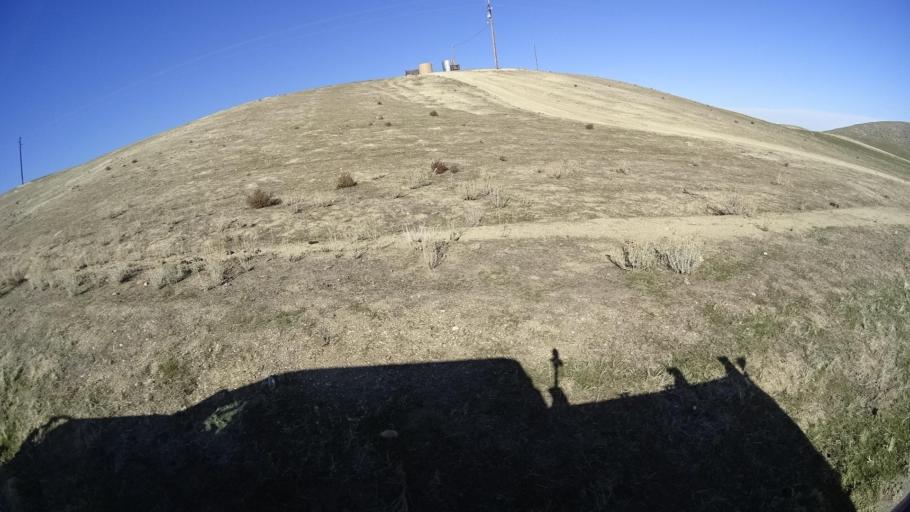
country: US
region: California
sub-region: Kern County
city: Taft Heights
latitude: 35.2318
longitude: -119.6633
